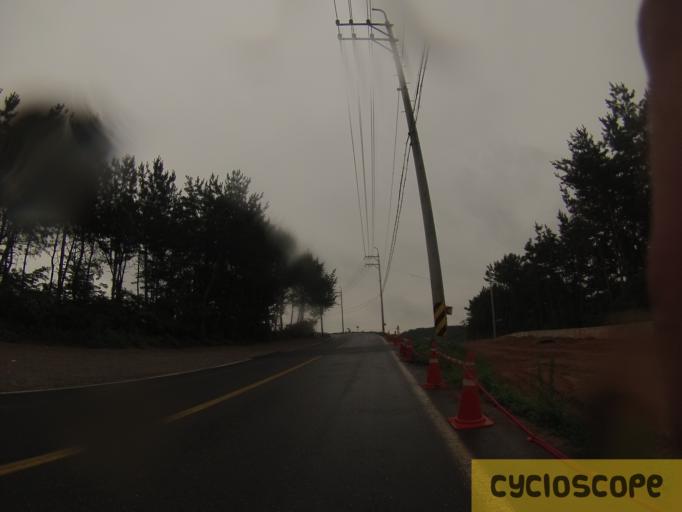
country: KR
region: Chungcheongnam-do
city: Taisen-ri
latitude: 36.1769
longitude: 126.5273
